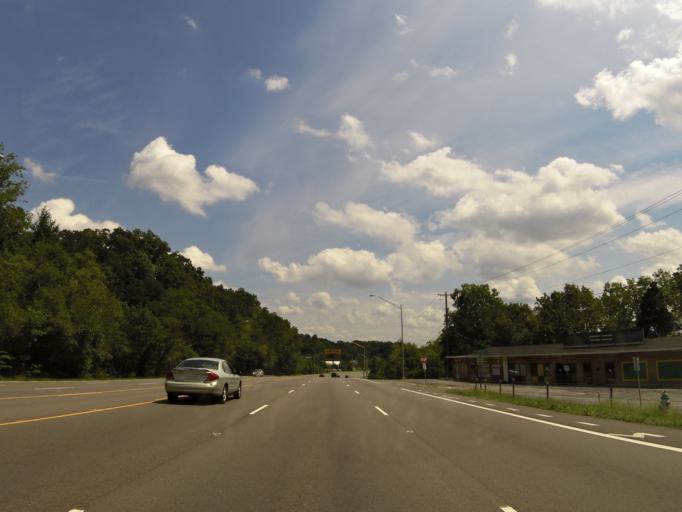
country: US
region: Tennessee
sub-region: Sullivan County
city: Kingsport
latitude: 36.5588
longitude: -82.5461
